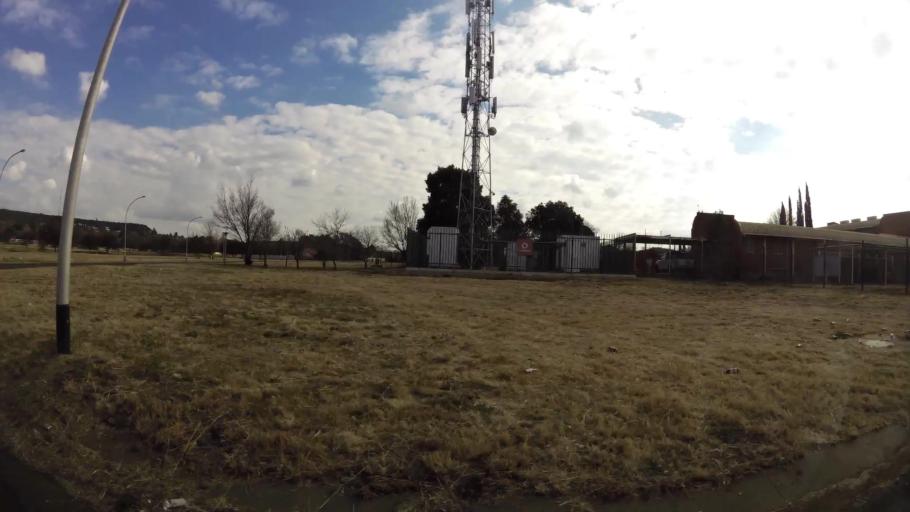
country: ZA
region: Orange Free State
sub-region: Mangaung Metropolitan Municipality
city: Bloemfontein
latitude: -29.0855
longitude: 26.2439
